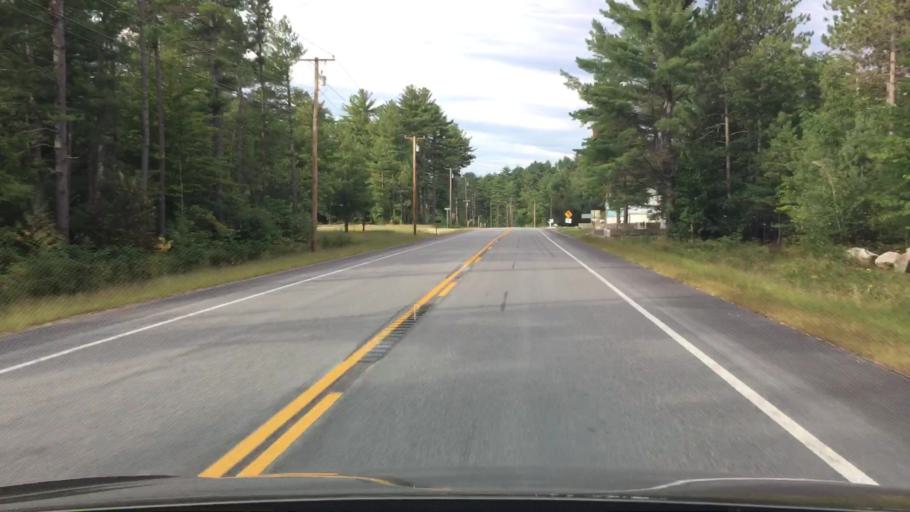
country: US
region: Maine
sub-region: Oxford County
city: Lovell
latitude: 44.0529
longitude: -70.8577
